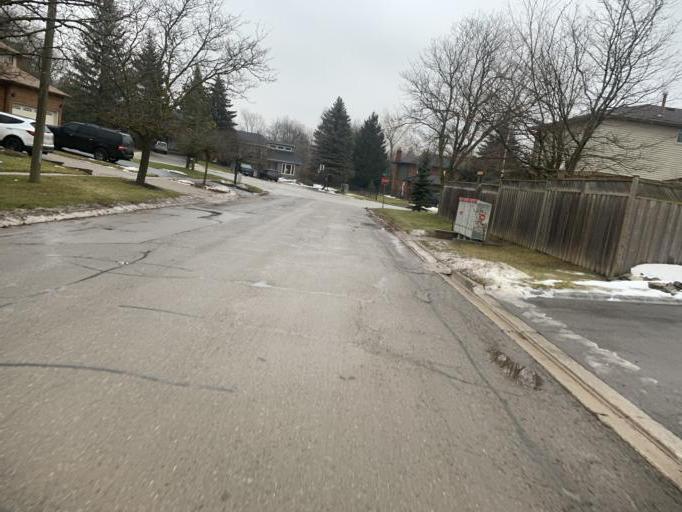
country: CA
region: Ontario
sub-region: Halton
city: Milton
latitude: 43.6588
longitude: -79.9285
